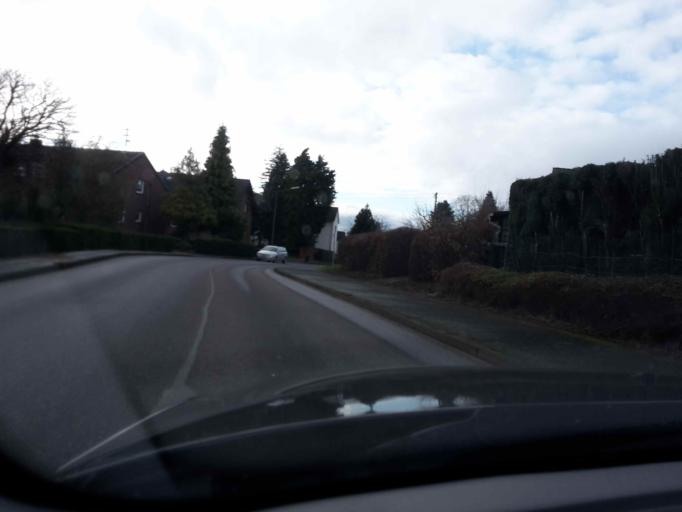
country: DE
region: North Rhine-Westphalia
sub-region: Regierungsbezirk Koln
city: Hennef
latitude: 50.7502
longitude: 7.2815
